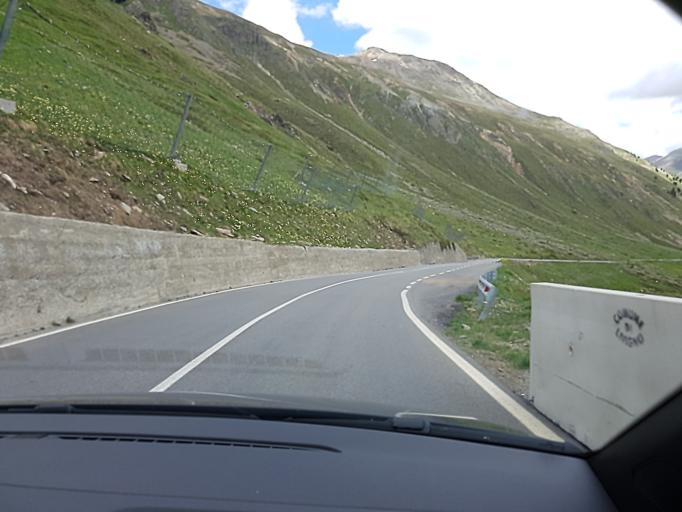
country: IT
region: Lombardy
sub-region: Provincia di Sondrio
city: Livigno
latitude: 46.4588
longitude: 10.0583
